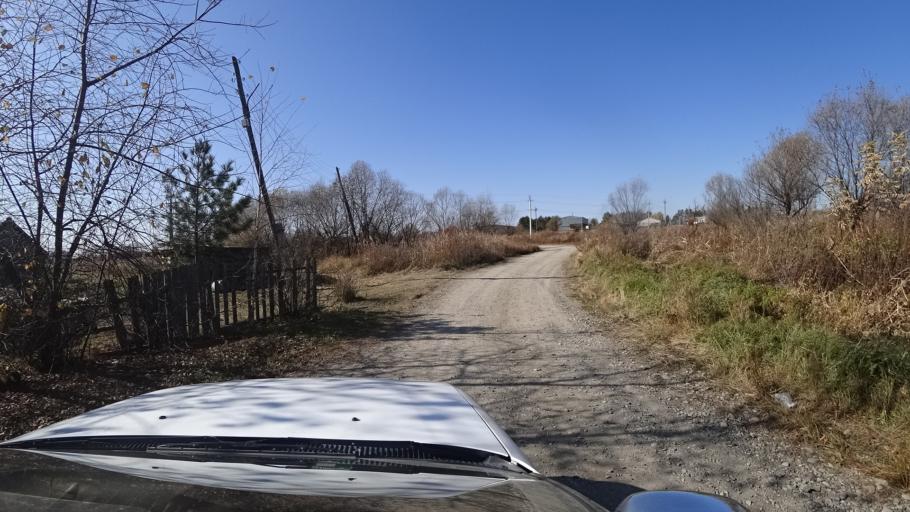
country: RU
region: Primorskiy
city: Dal'nerechensk
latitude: 45.9221
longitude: 133.7834
